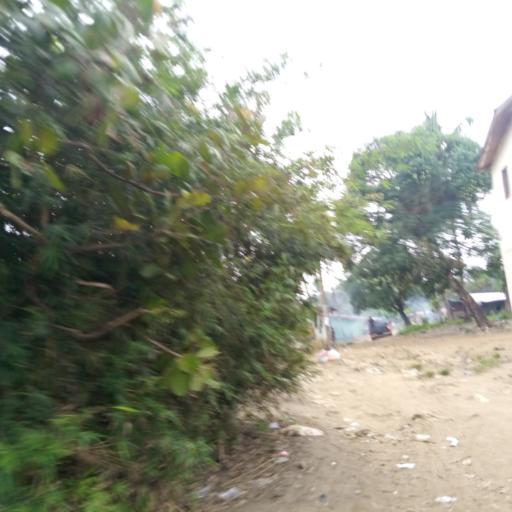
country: LR
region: Montserrado
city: Monrovia
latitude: 6.2989
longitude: -10.6866
